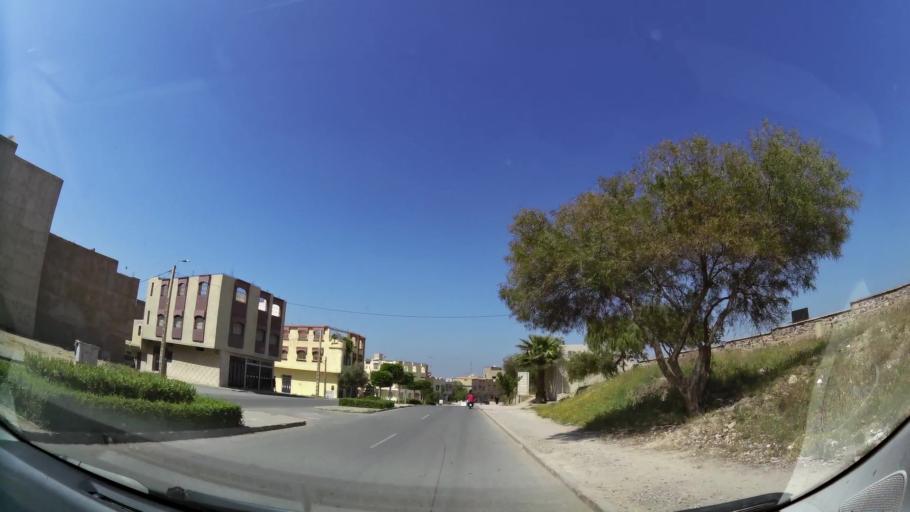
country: MA
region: Oriental
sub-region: Oujda-Angad
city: Oujda
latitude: 34.6860
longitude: -1.8812
